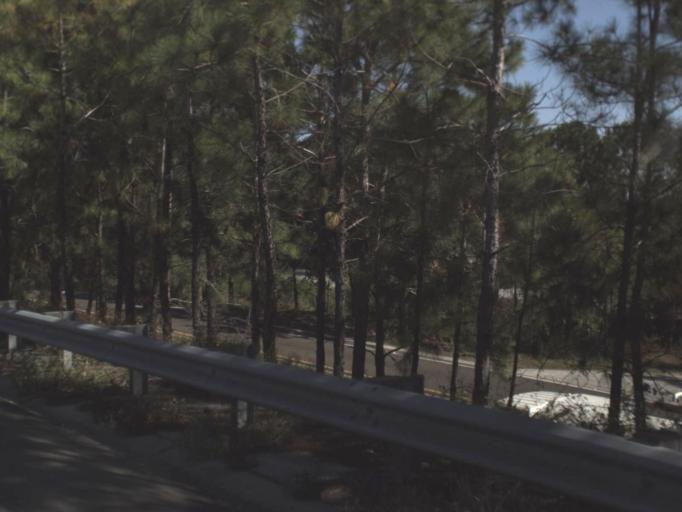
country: US
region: Florida
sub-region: Hillsborough County
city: Town 'n' Country
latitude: 27.9976
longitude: -82.5457
